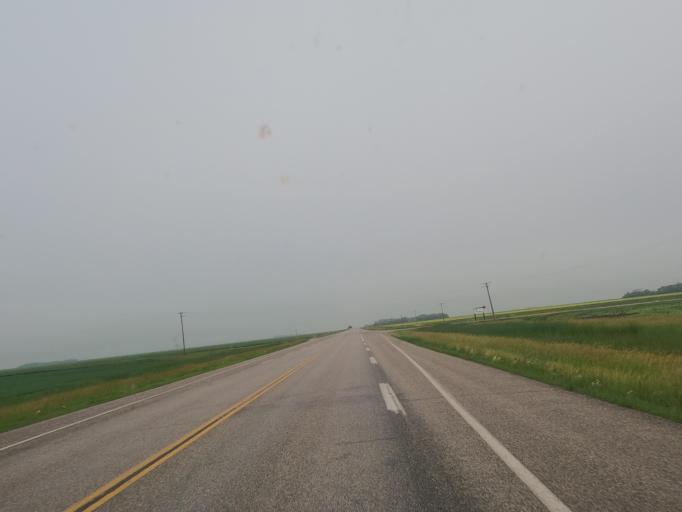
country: CA
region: Manitoba
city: Carman
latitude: 49.7391
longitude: -97.7989
